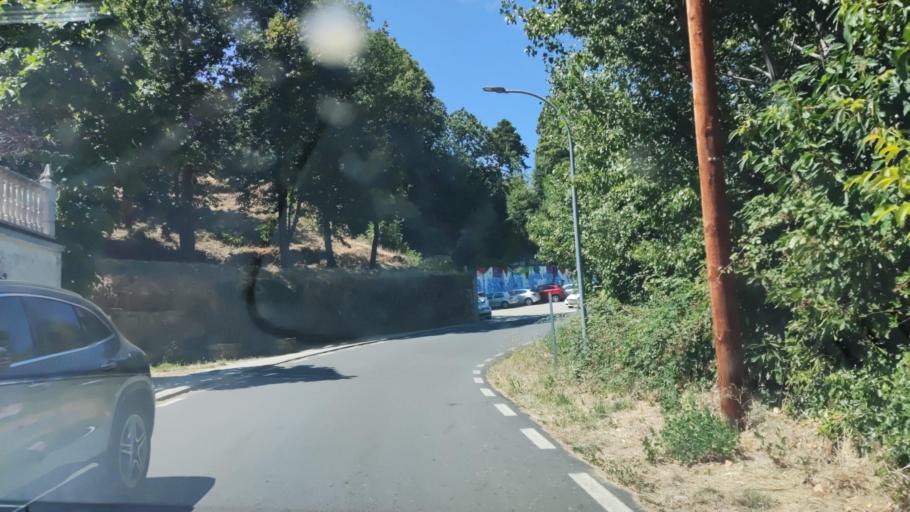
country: ES
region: Castille and Leon
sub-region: Provincia de Salamanca
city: Candelario
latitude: 40.3662
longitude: -5.7460
